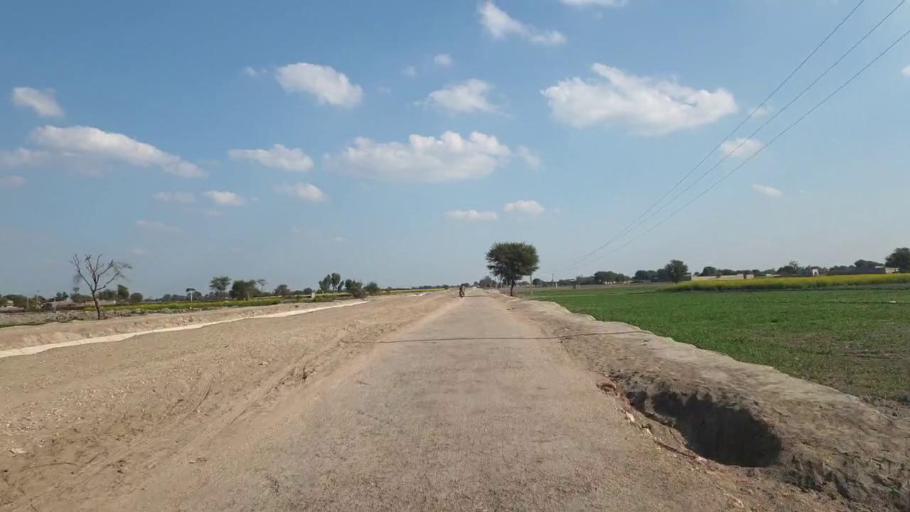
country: PK
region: Sindh
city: Shahpur Chakar
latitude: 26.1103
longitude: 68.5694
